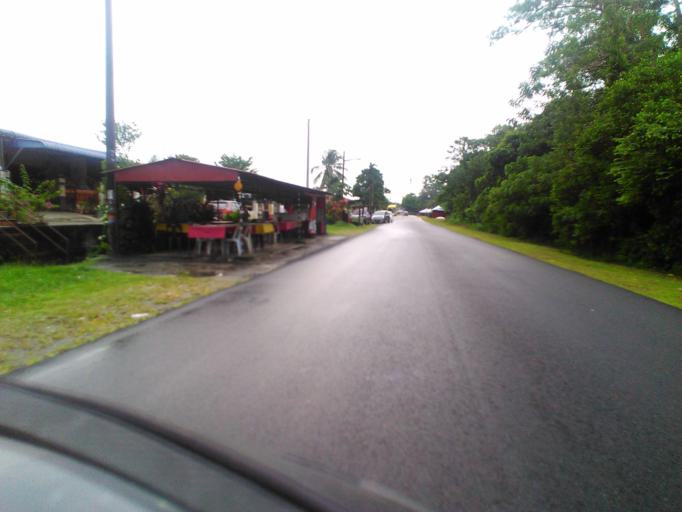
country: MY
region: Kedah
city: Kulim
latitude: 5.3659
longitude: 100.5749
